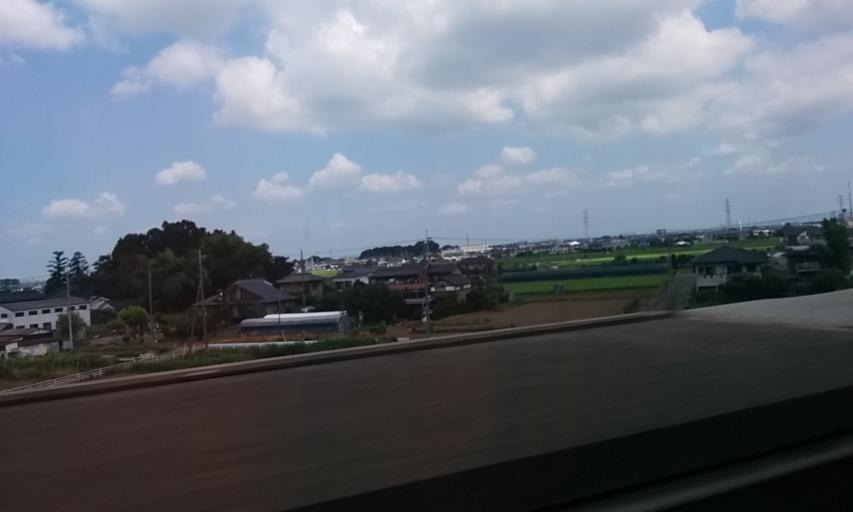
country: JP
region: Saitama
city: Kurihashi
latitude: 36.1439
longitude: 139.7236
